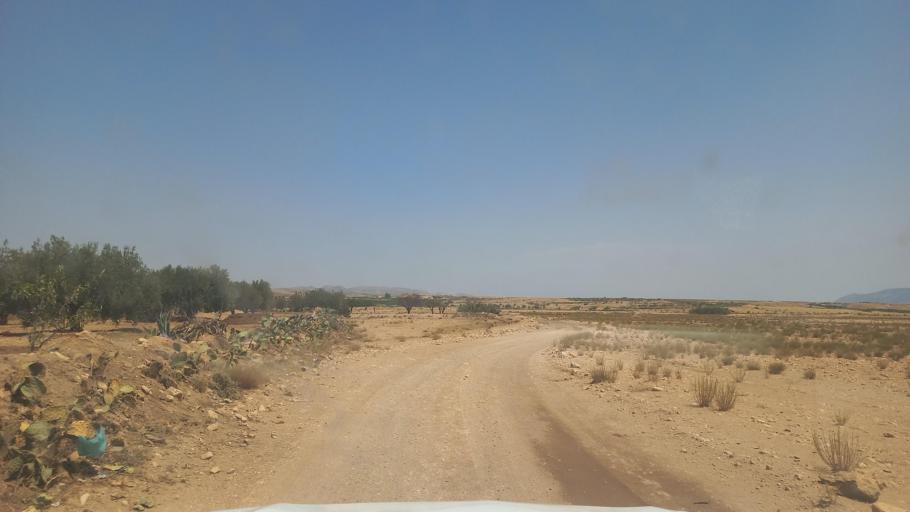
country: TN
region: Al Qasrayn
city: Kasserine
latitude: 35.2891
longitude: 8.9517
